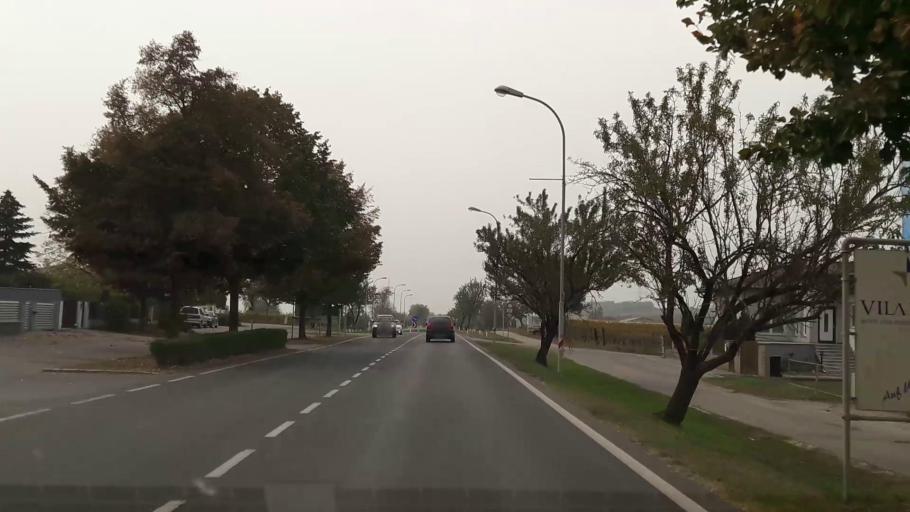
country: AT
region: Burgenland
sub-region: Politischer Bezirk Neusiedl am See
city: Gols
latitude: 47.9058
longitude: 16.8976
